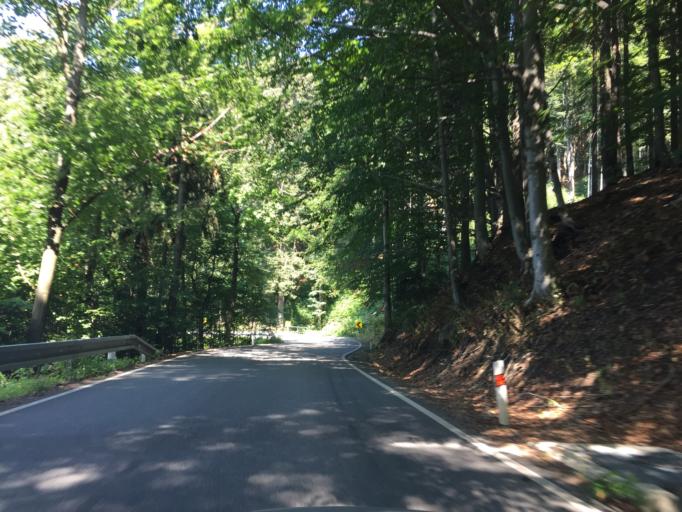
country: CZ
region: Liberecky
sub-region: Okres Jablonec nad Nisou
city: Janov nad Nisou
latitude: 50.7874
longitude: 15.1586
